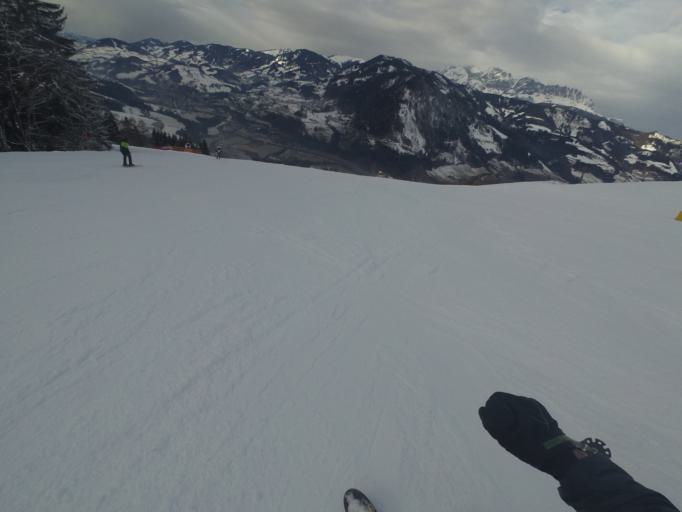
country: AT
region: Salzburg
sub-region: Politischer Bezirk Sankt Johann im Pongau
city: Sankt Johann im Pongau
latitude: 47.3197
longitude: 13.2050
